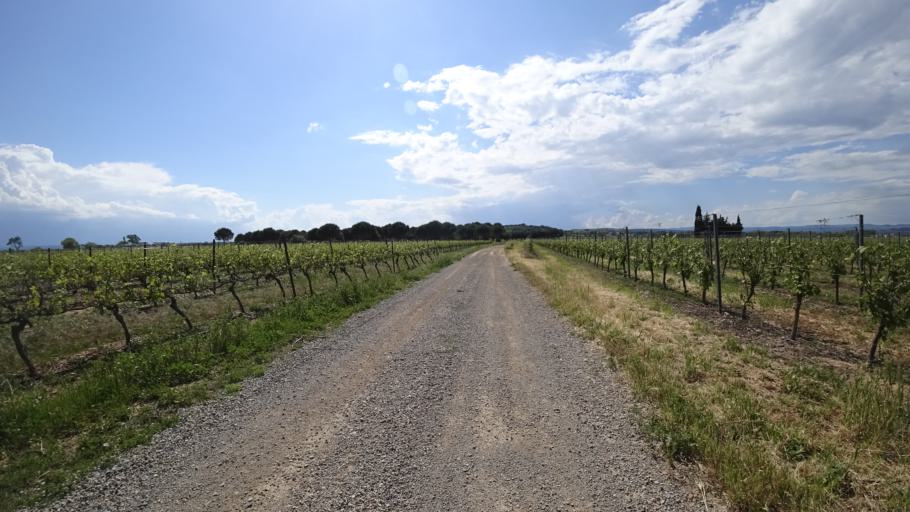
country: FR
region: Languedoc-Roussillon
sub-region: Departement de l'Aude
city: Ginestas
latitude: 43.2615
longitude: 2.8925
